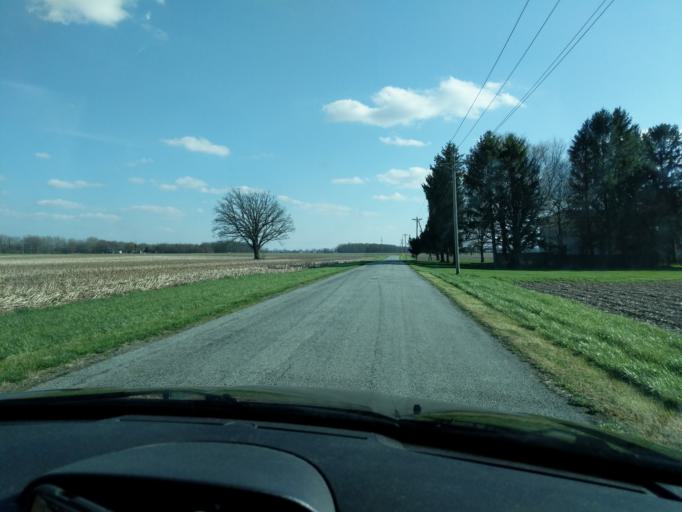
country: US
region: Ohio
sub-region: Champaign County
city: Urbana
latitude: 40.1407
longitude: -83.8156
